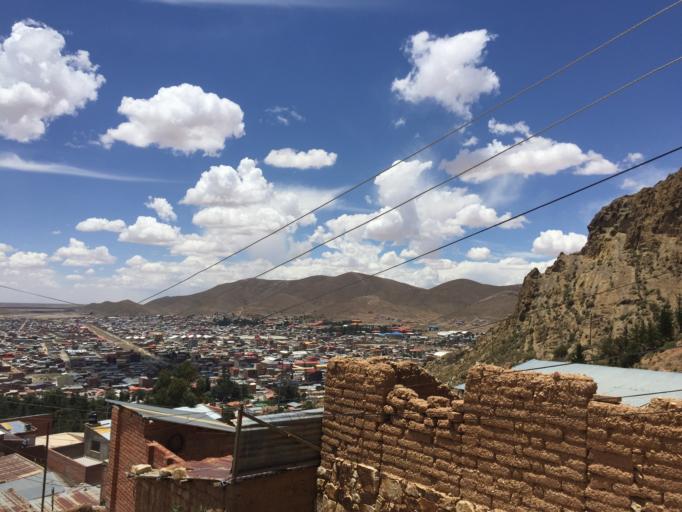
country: BO
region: Oruro
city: Oruro
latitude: -17.9766
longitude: -67.1215
